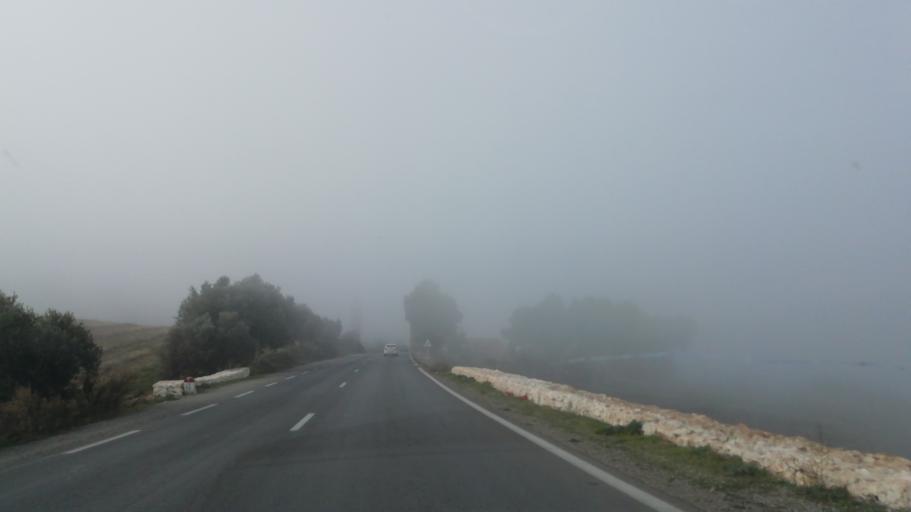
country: DZ
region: Mascara
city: Mascara
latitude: 35.5267
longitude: 0.3418
